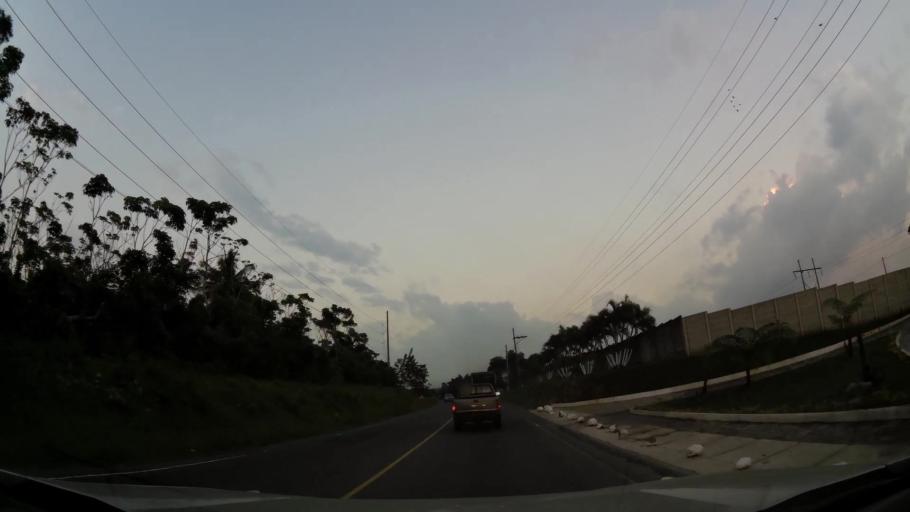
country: GT
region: Retalhuleu
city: San Felipe
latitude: 14.6132
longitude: -91.6017
